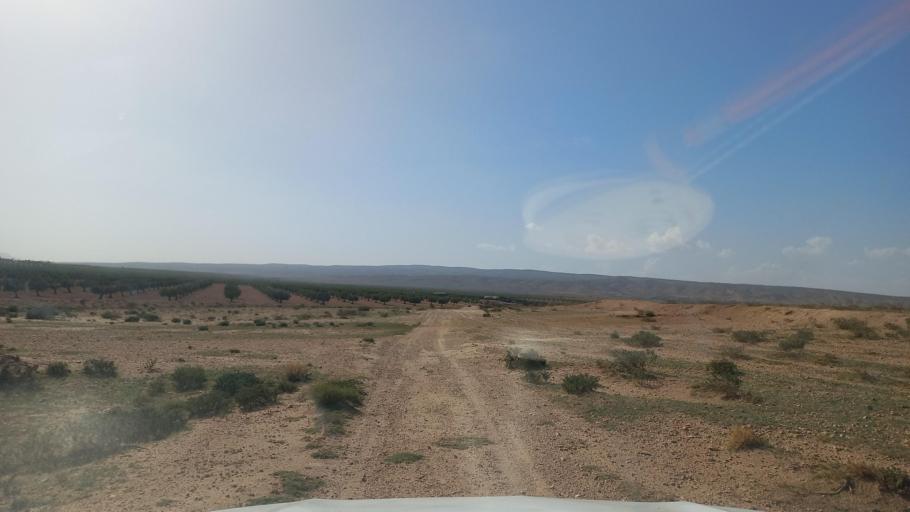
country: TN
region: Al Qasrayn
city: Kasserine
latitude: 35.3128
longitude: 9.0191
